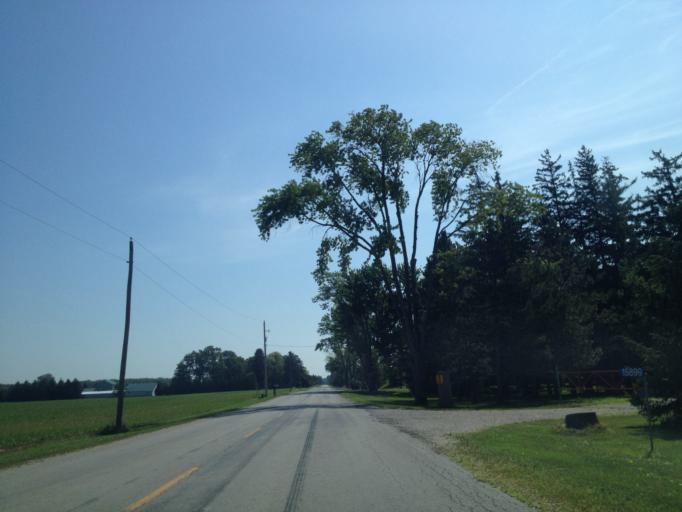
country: CA
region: Ontario
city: London
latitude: 43.1240
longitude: -81.2281
